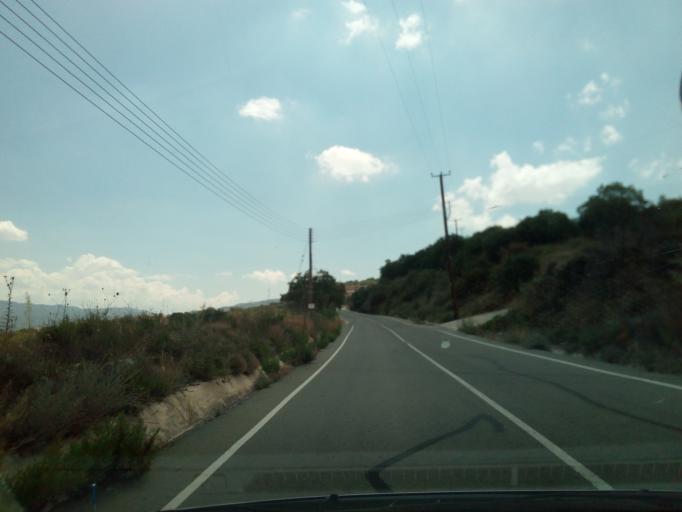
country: CY
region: Pafos
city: Polis
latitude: 34.9518
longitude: 32.4866
